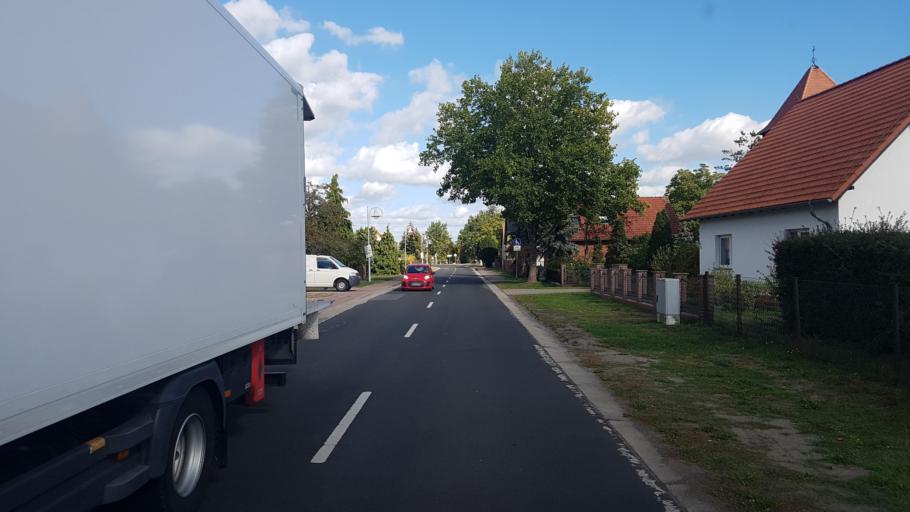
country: DE
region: Brandenburg
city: Peitz
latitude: 51.8124
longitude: 14.4241
